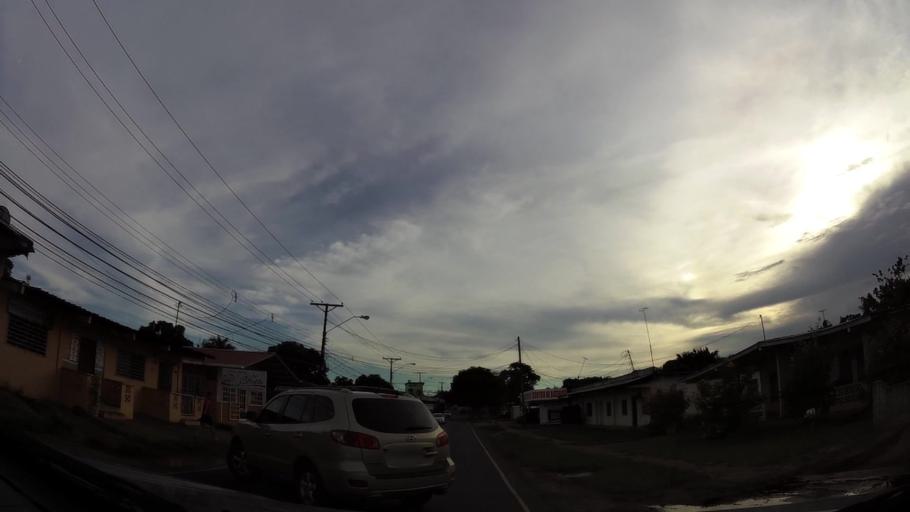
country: PA
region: Panama
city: La Chorrera
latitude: 8.8866
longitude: -79.7794
